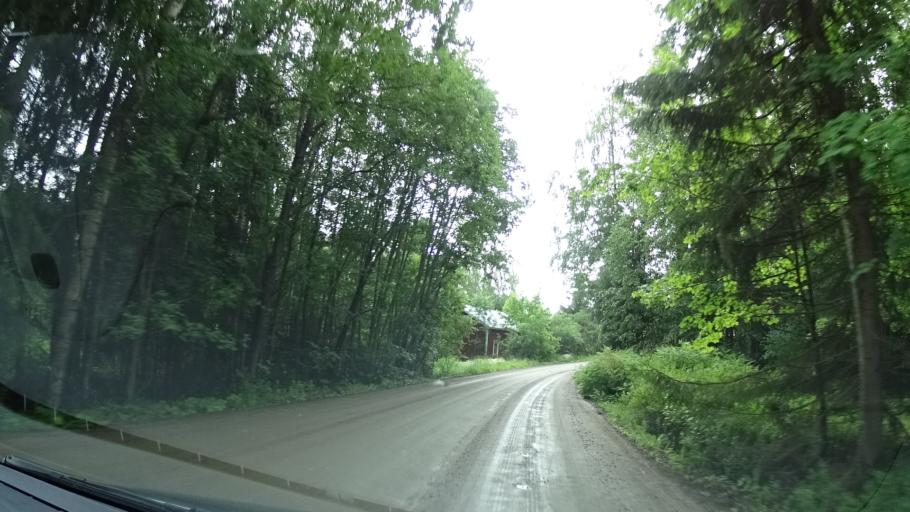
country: FI
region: Pirkanmaa
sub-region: Lounais-Pirkanmaa
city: Punkalaidun
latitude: 61.1036
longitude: 23.2796
